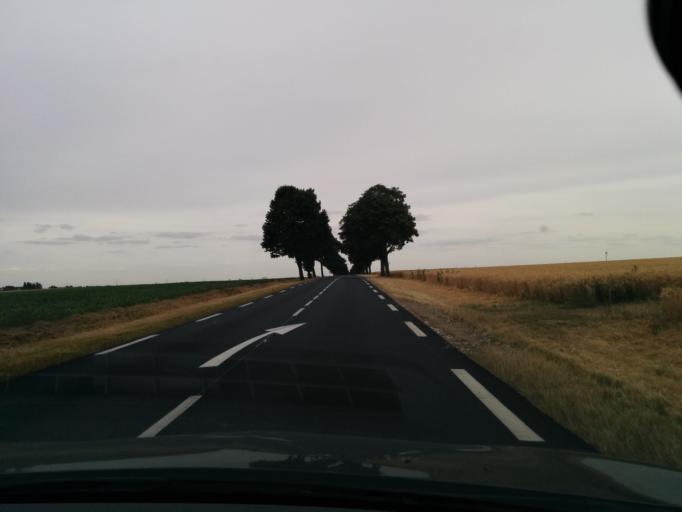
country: FR
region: Ile-de-France
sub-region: Departement de l'Essonne
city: Pussay
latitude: 48.3990
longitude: 1.9712
